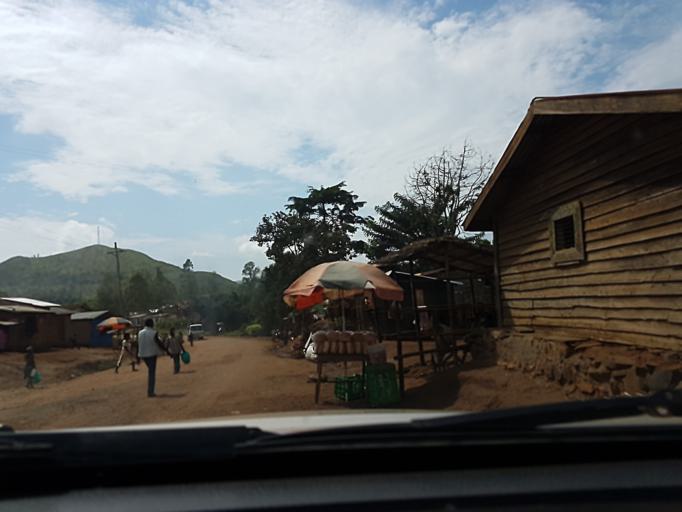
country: CD
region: South Kivu
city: Bukavu
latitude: -2.6615
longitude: 28.8741
